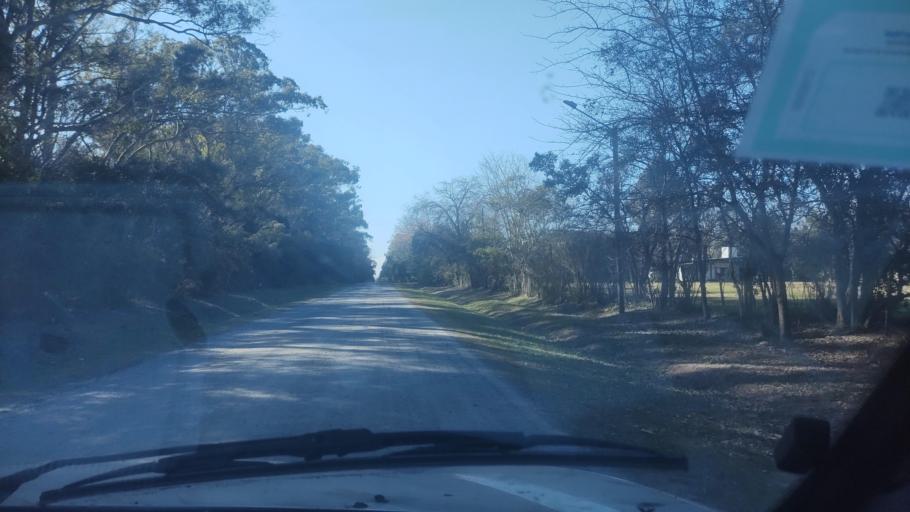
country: AR
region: Buenos Aires
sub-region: Partido de La Plata
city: La Plata
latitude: -34.8531
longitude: -58.1058
